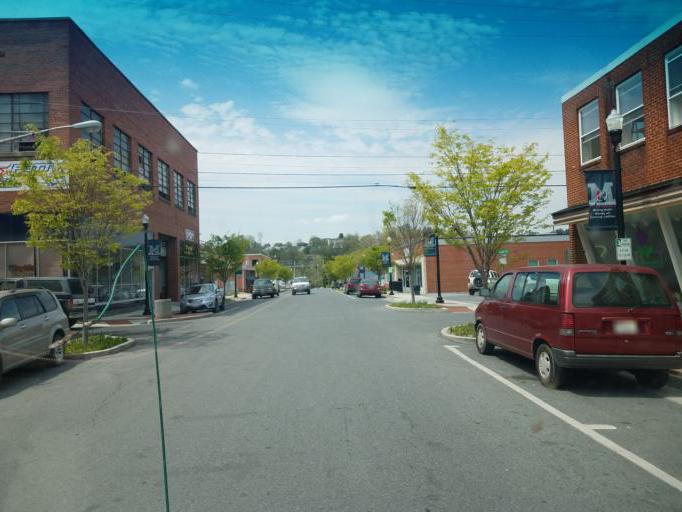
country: US
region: Virginia
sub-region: Smyth County
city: Marion
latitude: 36.8342
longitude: -81.5178
